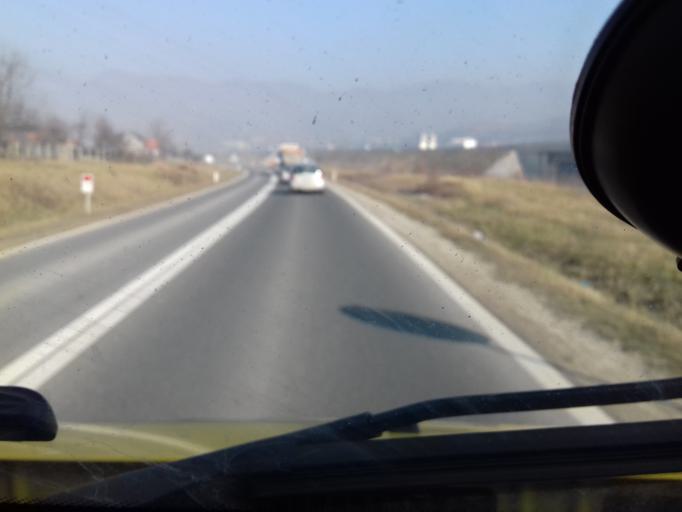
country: BA
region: Federation of Bosnia and Herzegovina
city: Zenica
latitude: 44.1684
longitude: 17.9699
